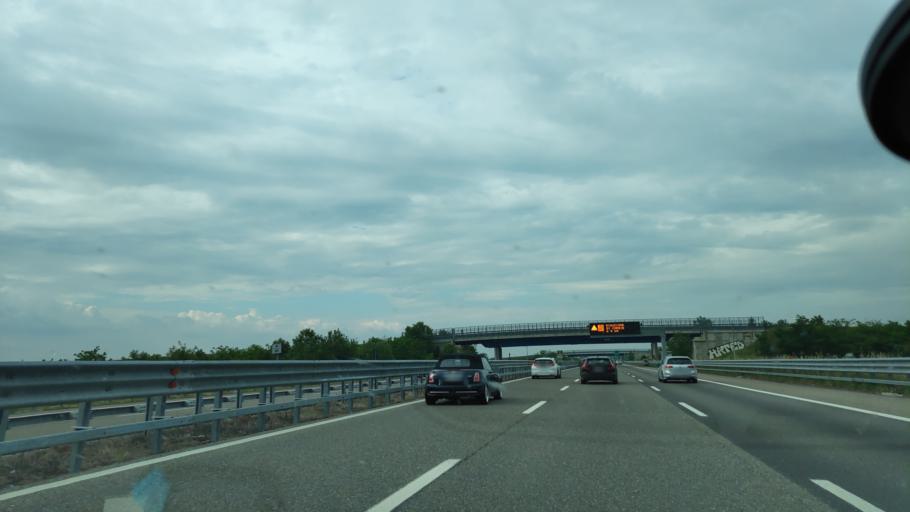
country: IT
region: Lombardy
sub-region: Provincia di Pavia
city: Casei
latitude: 45.0021
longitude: 8.9151
